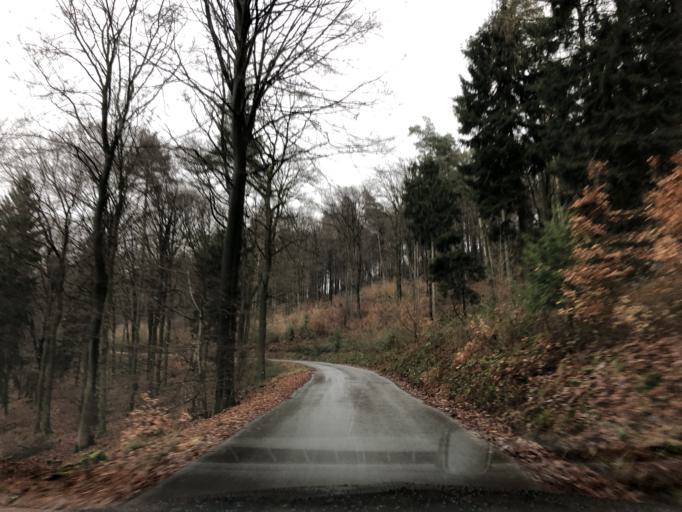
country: DE
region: Baden-Wuerttemberg
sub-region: Karlsruhe Region
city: Dossenheim
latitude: 49.4494
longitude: 8.7045
